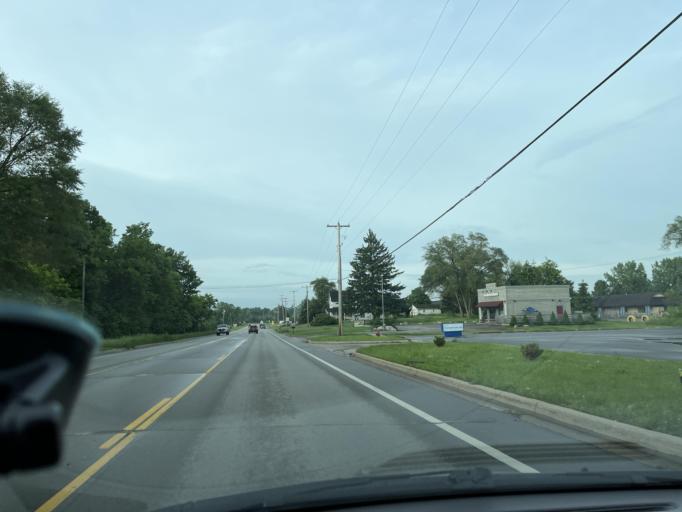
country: US
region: Michigan
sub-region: Barry County
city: Middleville
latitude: 42.7079
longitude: -85.4701
